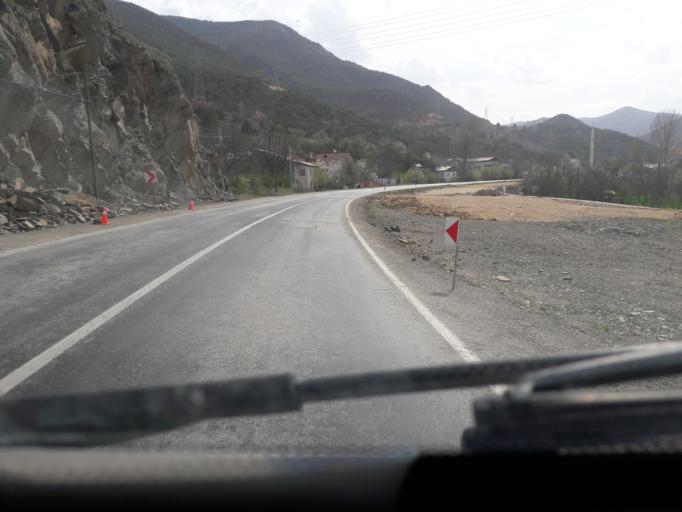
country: TR
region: Gumushane
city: Kale
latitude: 40.3984
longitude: 39.6057
